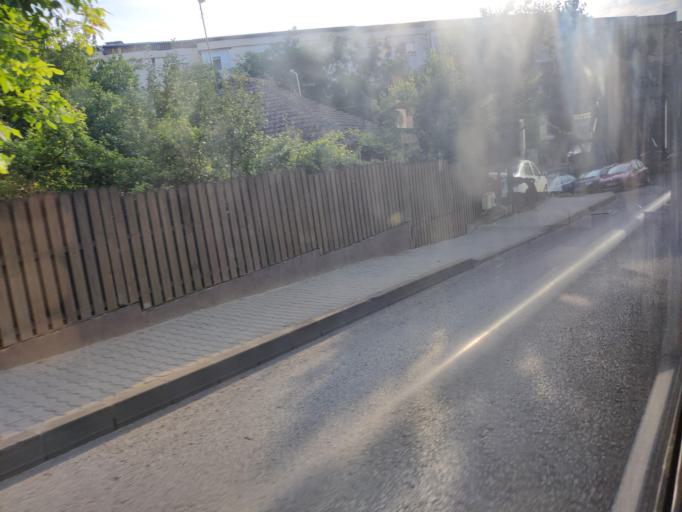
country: RO
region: Iasi
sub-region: Municipiul Iasi
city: Iasi
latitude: 47.1664
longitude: 27.5965
